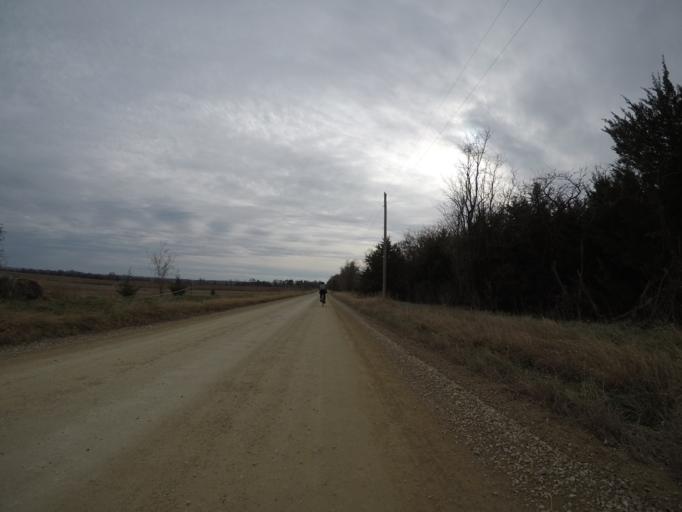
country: US
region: Kansas
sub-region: Riley County
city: Ogden
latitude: 39.1653
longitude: -96.6819
